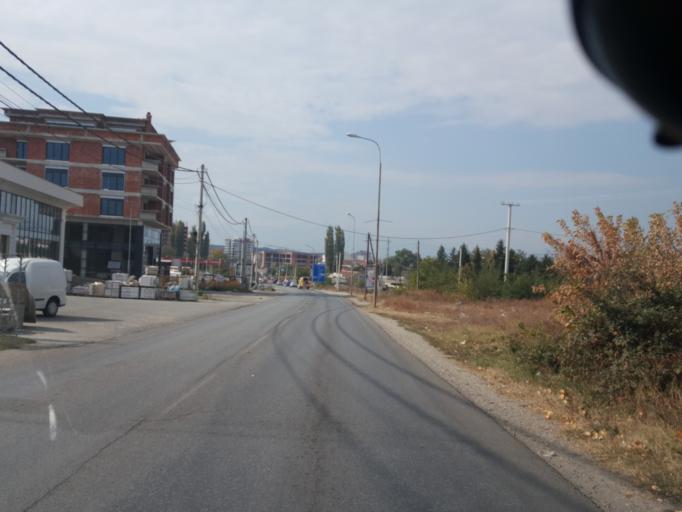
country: XK
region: Gjakova
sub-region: Komuna e Gjakoves
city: Gjakove
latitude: 42.3733
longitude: 20.4479
